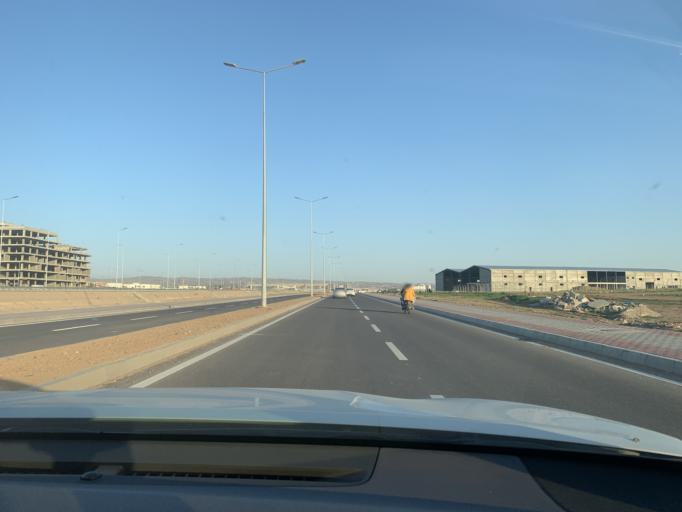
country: IQ
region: Arbil
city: Erbil
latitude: 36.2845
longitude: 44.0505
